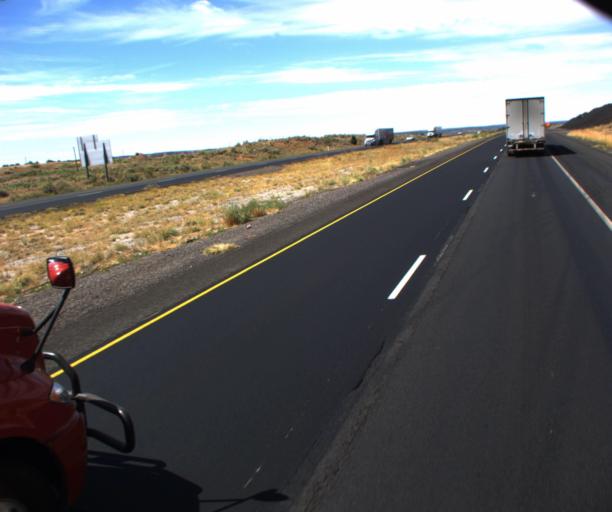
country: US
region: Arizona
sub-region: Apache County
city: Houck
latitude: 35.3179
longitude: -109.0926
